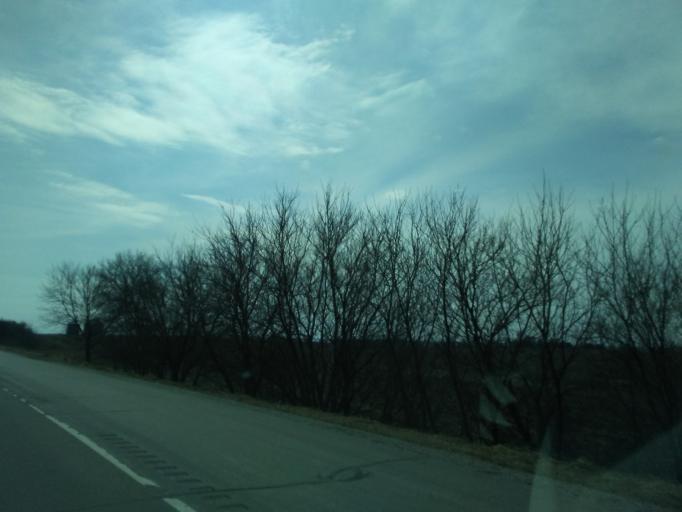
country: US
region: Minnesota
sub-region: Fillmore County
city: Harmony
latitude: 43.5068
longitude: -91.8712
